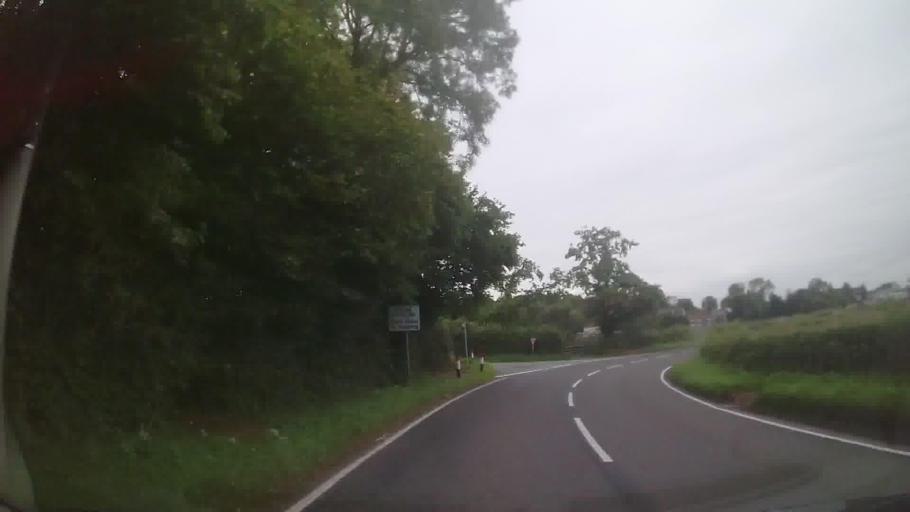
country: GB
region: Wales
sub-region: Carmarthenshire
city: Saint Clears
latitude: 51.8079
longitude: -4.4985
